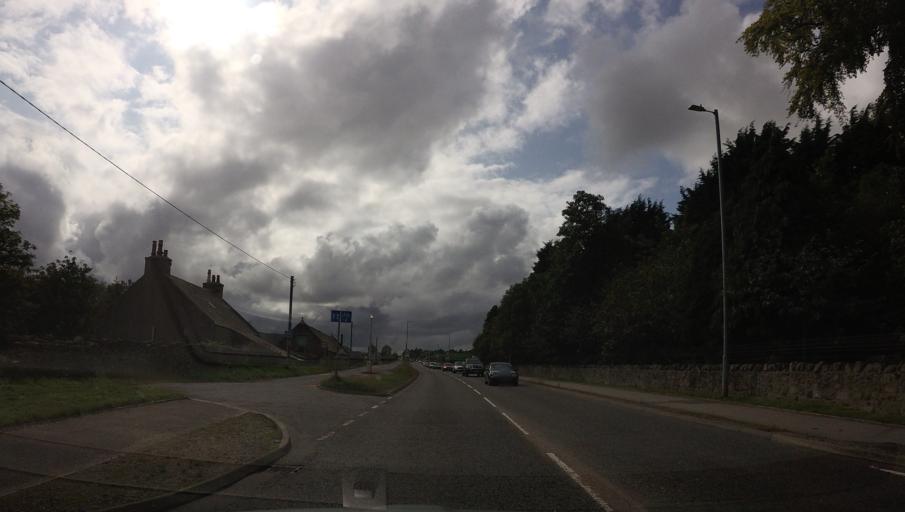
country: GB
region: Scotland
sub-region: Aberdeen City
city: Cults
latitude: 57.1505
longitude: -2.1838
